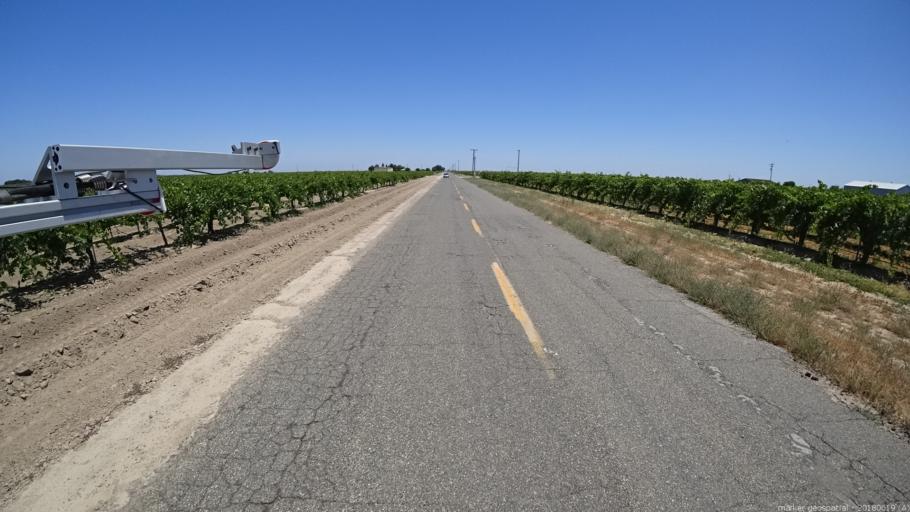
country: US
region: California
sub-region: Madera County
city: Parkwood
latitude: 36.8658
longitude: -120.0983
